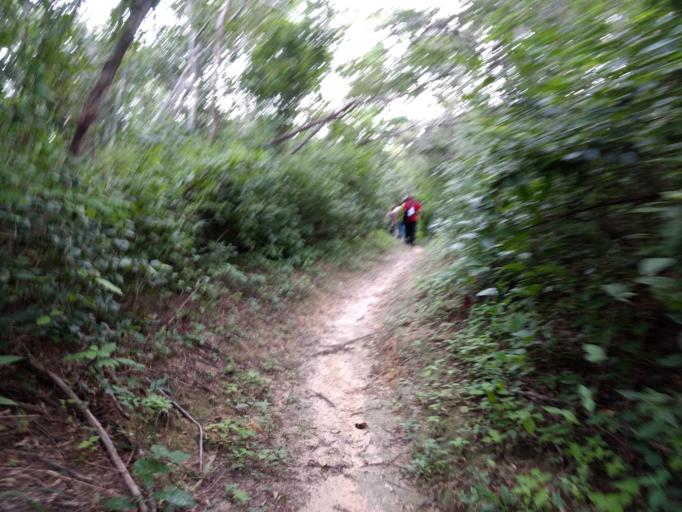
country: BR
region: Ceara
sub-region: Crateus
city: Crateus
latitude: -5.1425
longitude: -40.9210
